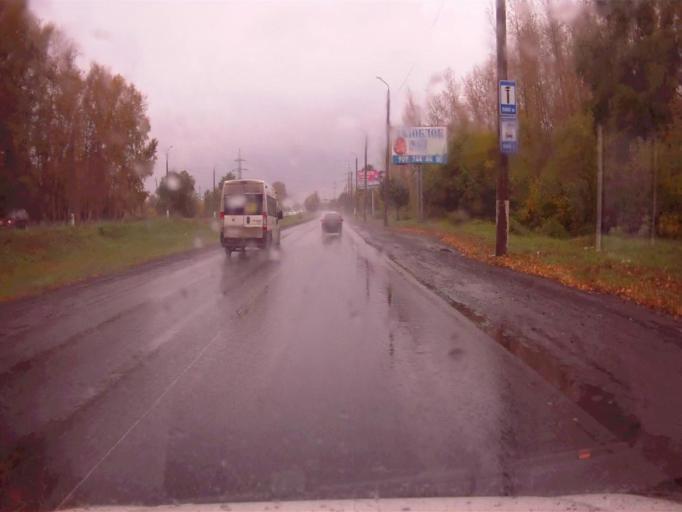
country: RU
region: Chelyabinsk
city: Dolgoderevenskoye
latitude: 55.2445
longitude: 61.3598
